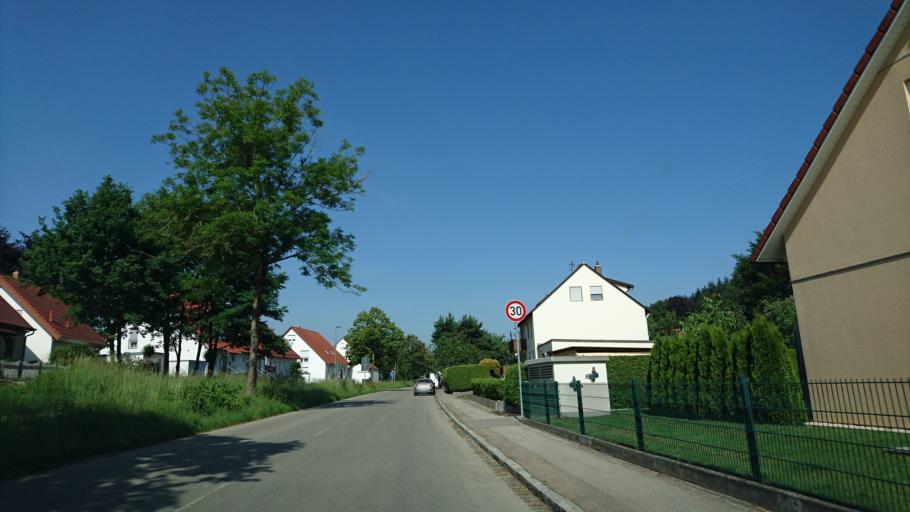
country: DE
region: Bavaria
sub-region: Swabia
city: Diedorf
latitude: 48.3567
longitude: 10.7580
